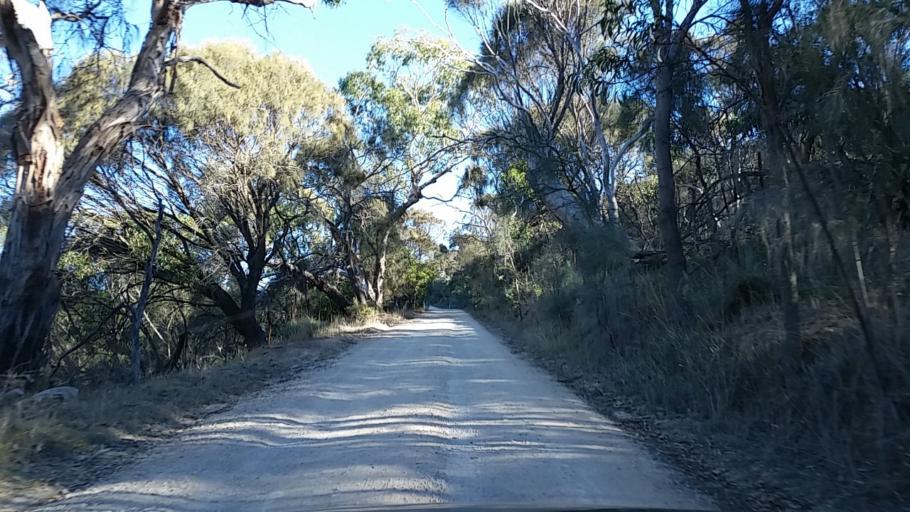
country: AU
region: South Australia
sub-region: Mount Barker
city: Nairne
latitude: -35.0629
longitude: 138.9240
